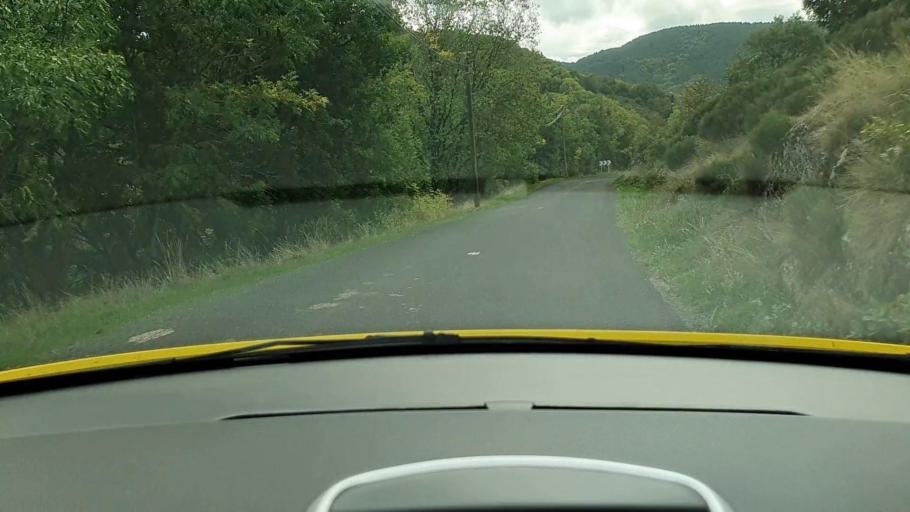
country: FR
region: Languedoc-Roussillon
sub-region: Departement de la Lozere
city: Meyrueis
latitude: 44.0704
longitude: 3.4521
